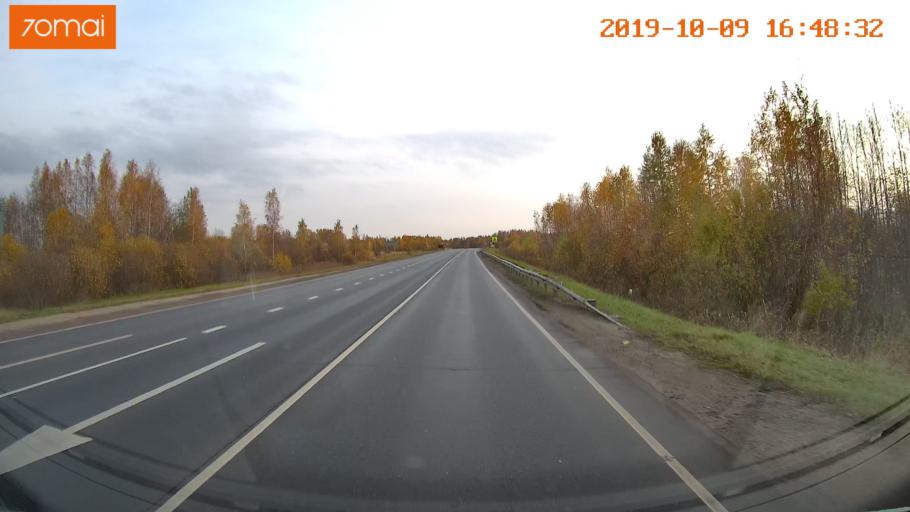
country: RU
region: Kostroma
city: Volgorechensk
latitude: 57.4272
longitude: 41.1904
